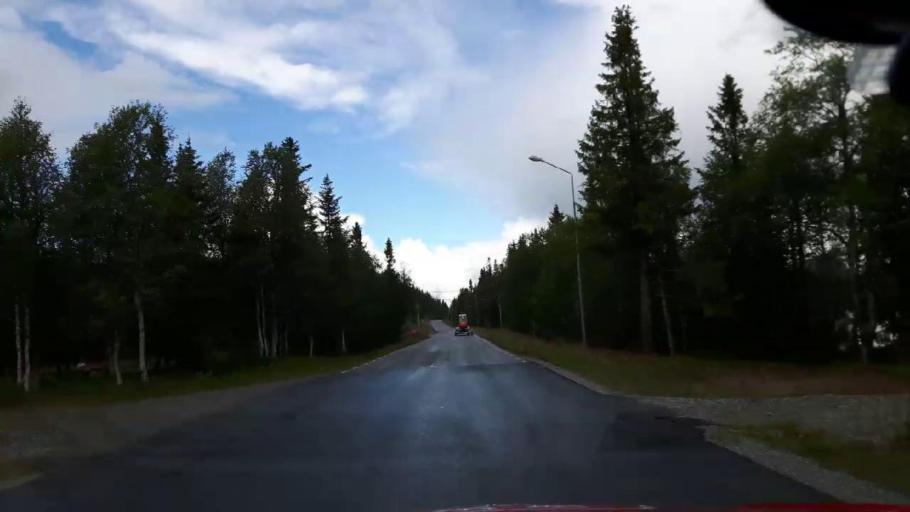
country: SE
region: Vaesterbotten
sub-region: Vilhelmina Kommun
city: Sjoberg
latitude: 64.9735
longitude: 15.3307
